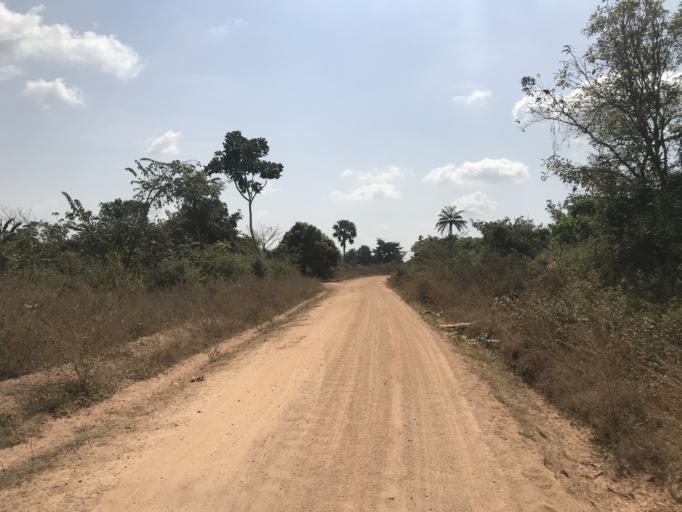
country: NG
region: Osun
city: Ifon
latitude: 7.9475
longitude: 4.4924
